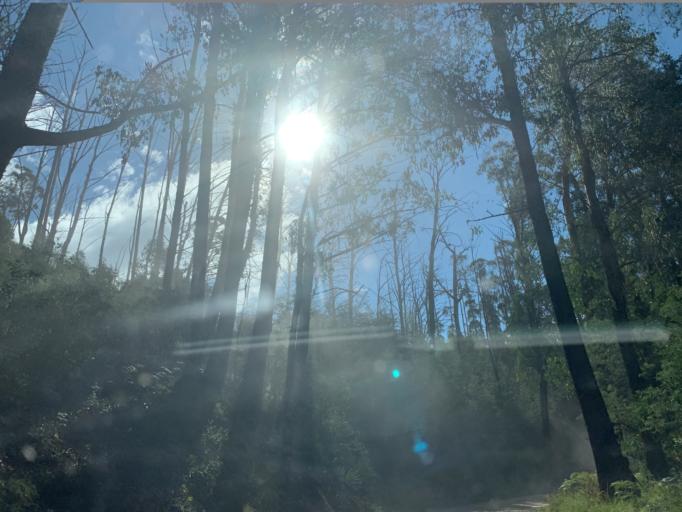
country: AU
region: Victoria
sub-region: Mansfield
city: Mansfield
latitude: -37.0984
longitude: 146.4671
